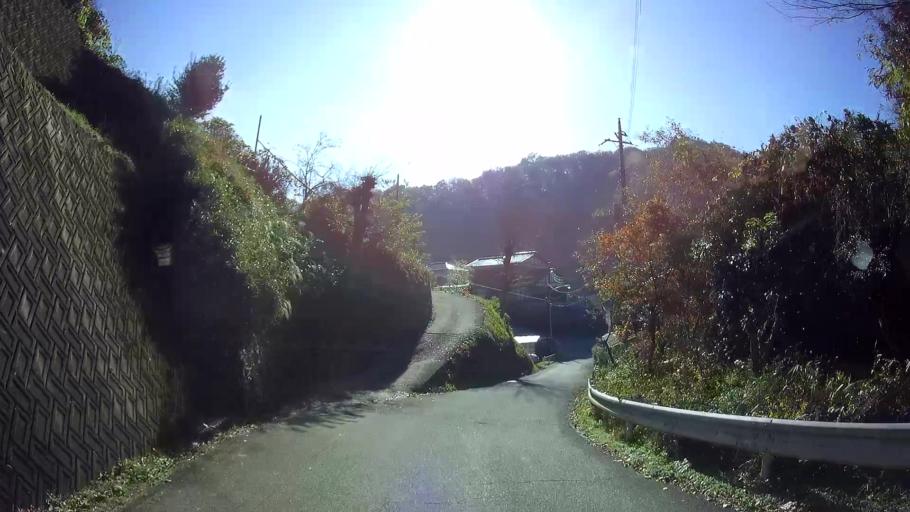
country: JP
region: Yamanashi
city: Uenohara
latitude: 35.5941
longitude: 139.1255
